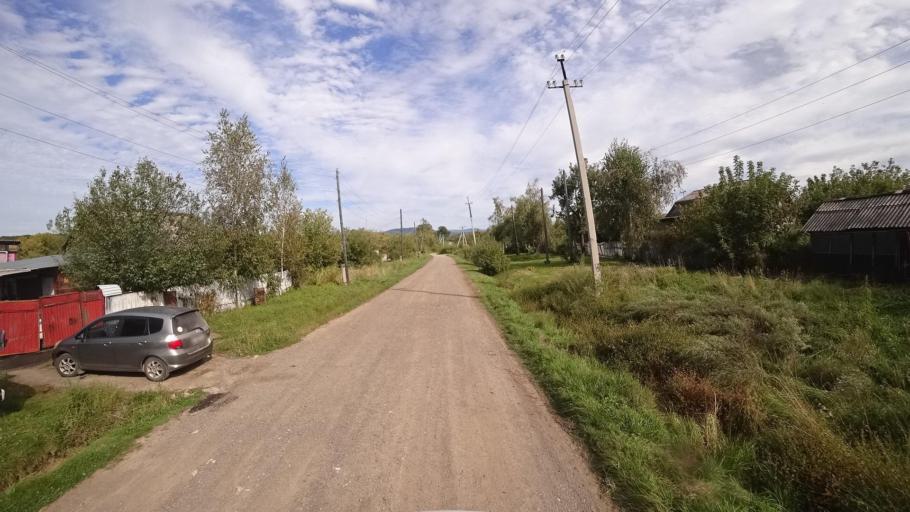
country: RU
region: Primorskiy
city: Dostoyevka
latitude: 44.3286
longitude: 133.4827
